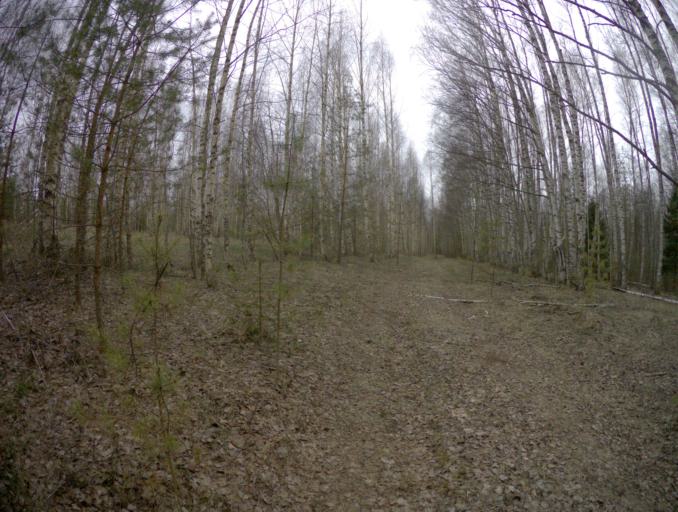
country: RU
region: Vladimir
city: Sudogda
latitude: 56.0374
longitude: 40.7919
